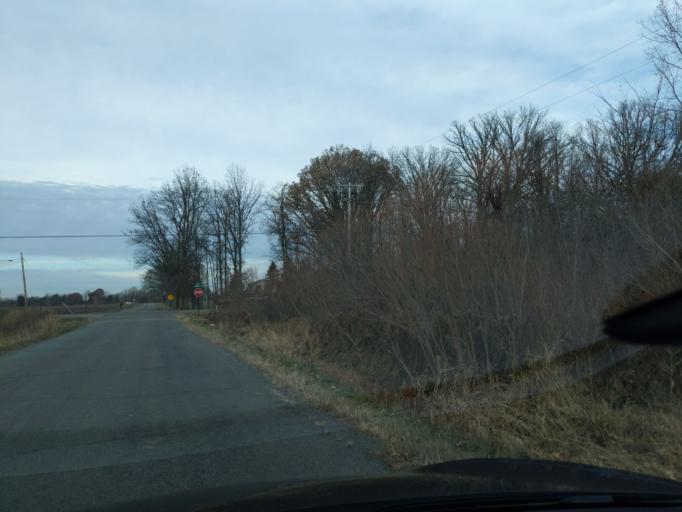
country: US
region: Michigan
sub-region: Ingham County
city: Okemos
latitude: 42.6686
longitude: -84.3834
